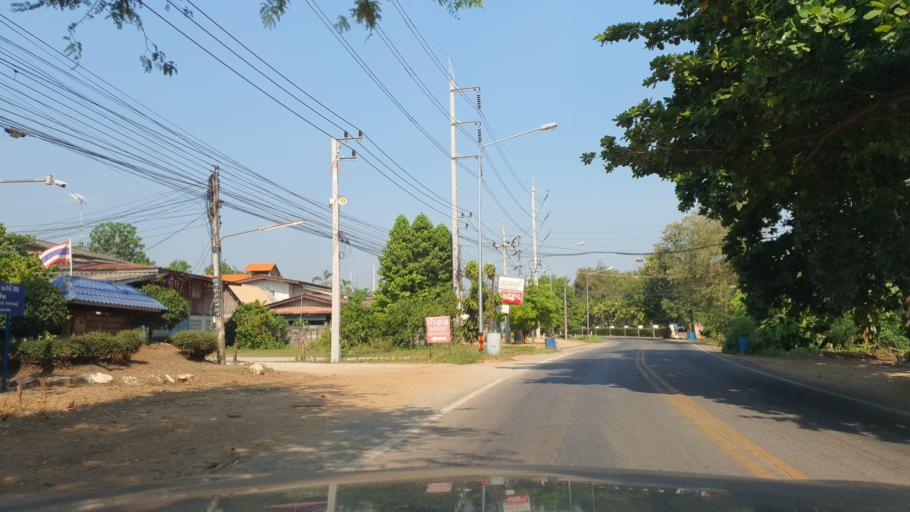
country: TH
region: Kanchanaburi
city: Kanchanaburi
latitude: 14.0367
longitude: 99.4883
